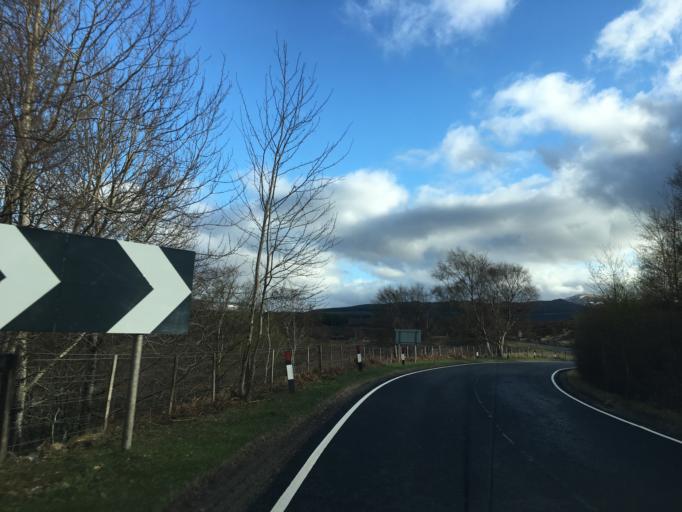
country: GB
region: Scotland
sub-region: Highland
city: Kingussie
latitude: 56.9940
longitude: -4.2485
